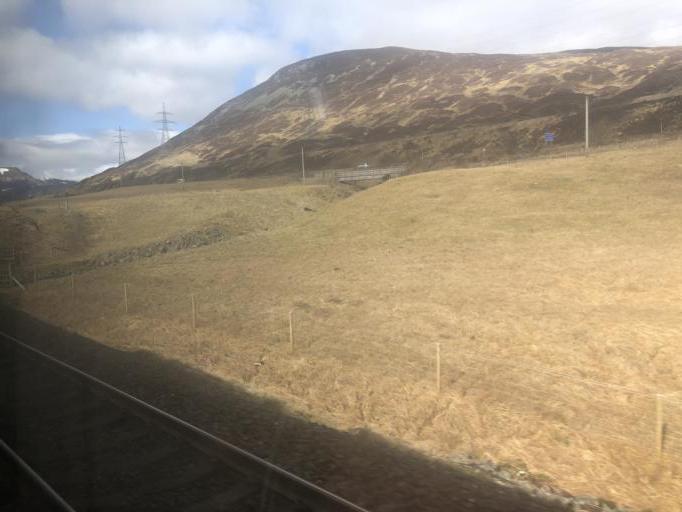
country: GB
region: Scotland
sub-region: Highland
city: Kingussie
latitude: 56.8239
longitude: -4.2026
